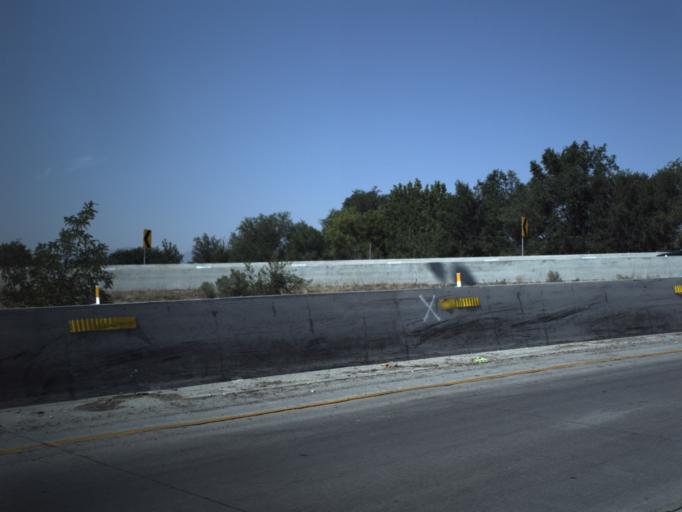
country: US
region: Utah
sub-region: Salt Lake County
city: Midvale
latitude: 40.6367
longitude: -111.9063
